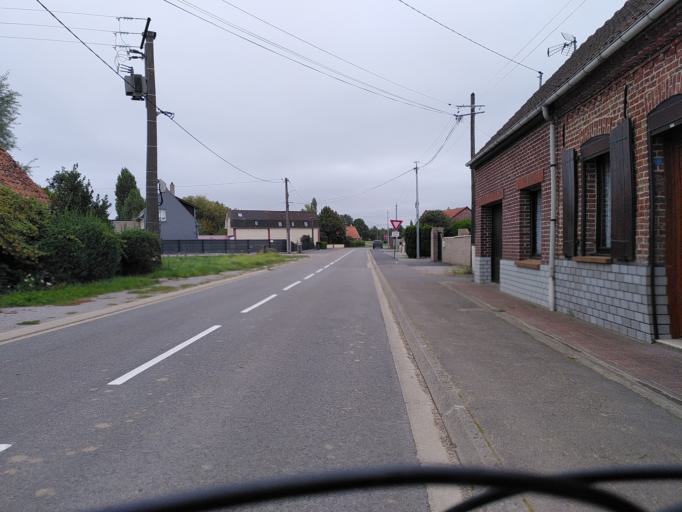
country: FR
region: Nord-Pas-de-Calais
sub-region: Departement du Pas-de-Calais
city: Isbergues
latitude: 50.6341
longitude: 2.4339
